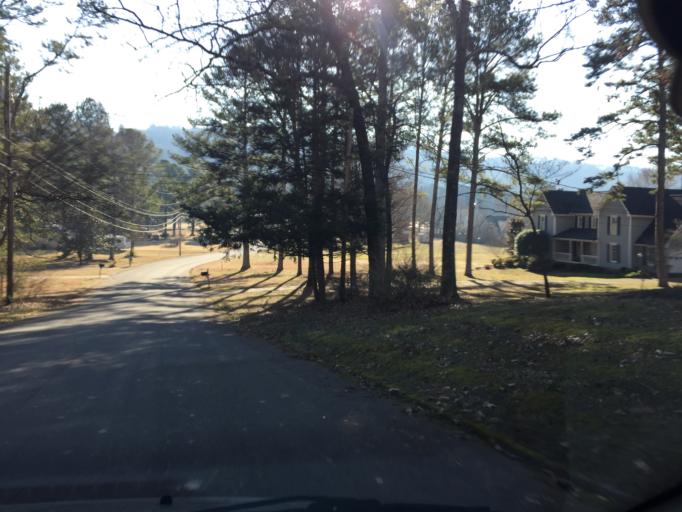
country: US
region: Tennessee
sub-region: Hamilton County
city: Collegedale
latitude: 35.0339
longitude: -85.0830
